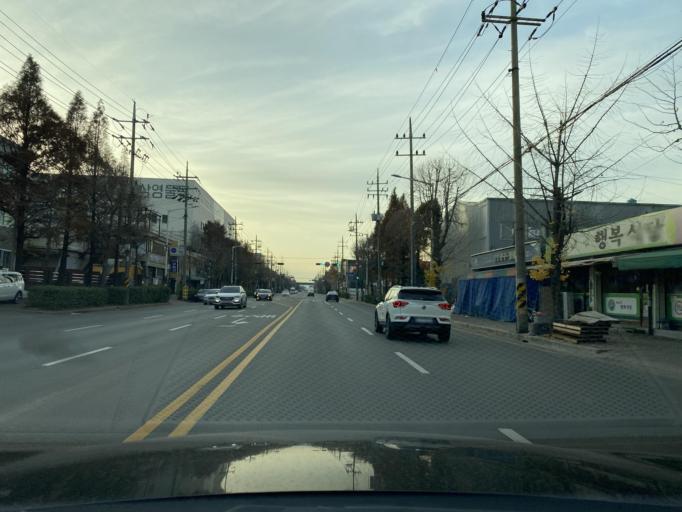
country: KR
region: Incheon
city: Incheon
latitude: 37.4992
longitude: 126.6553
